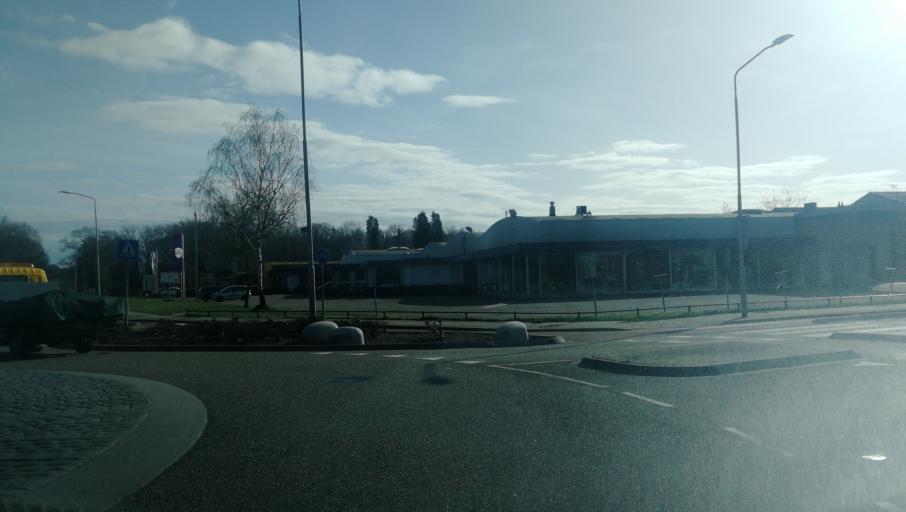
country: NL
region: Limburg
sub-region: Gemeente Venlo
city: Venlo
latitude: 51.3566
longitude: 6.1617
